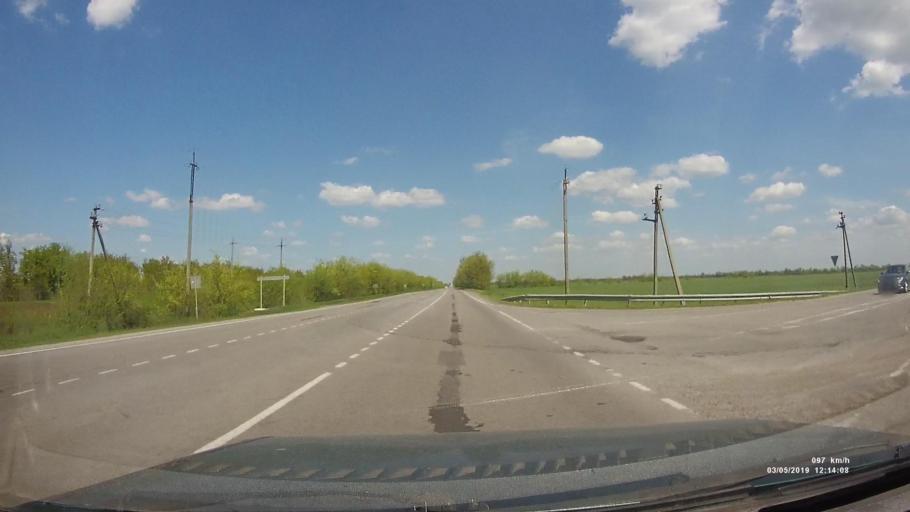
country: RU
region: Rostov
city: Melikhovskaya
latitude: 47.3400
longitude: 40.5604
